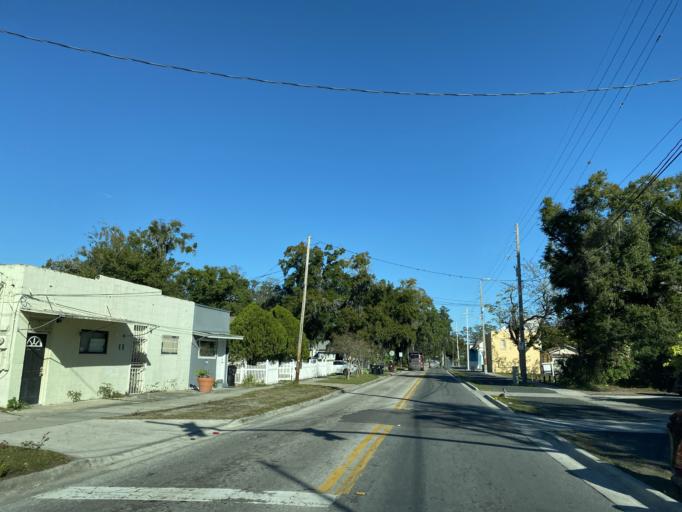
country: US
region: Florida
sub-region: Orange County
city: Orlando
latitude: 28.5458
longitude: -81.3932
